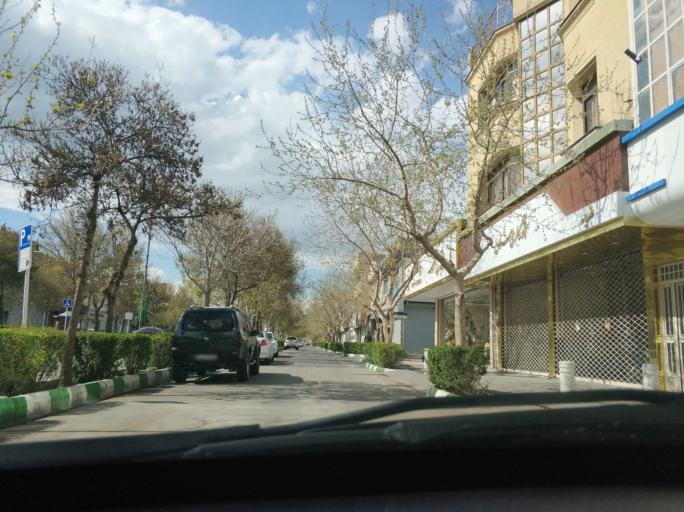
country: IR
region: Razavi Khorasan
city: Mashhad
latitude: 36.2718
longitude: 59.5952
